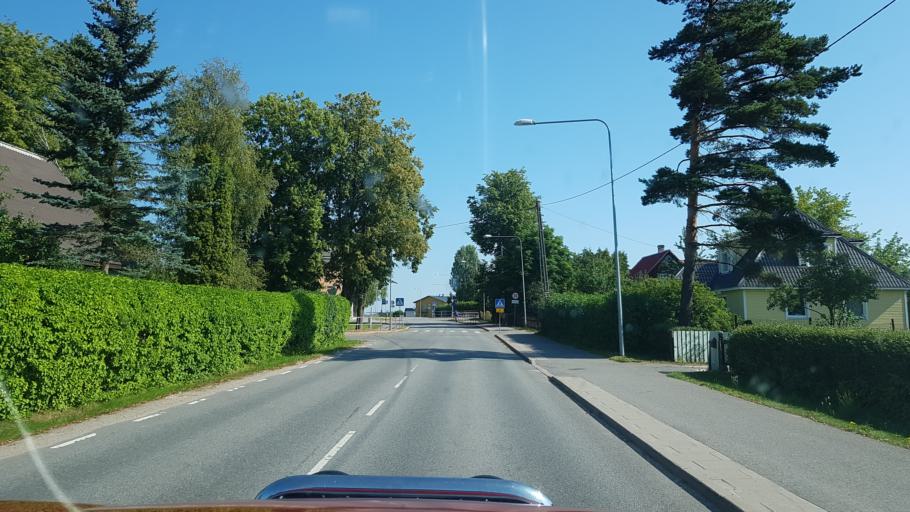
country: EE
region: Tartu
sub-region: Tartu linn
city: Tartu
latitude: 58.4229
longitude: 26.7631
